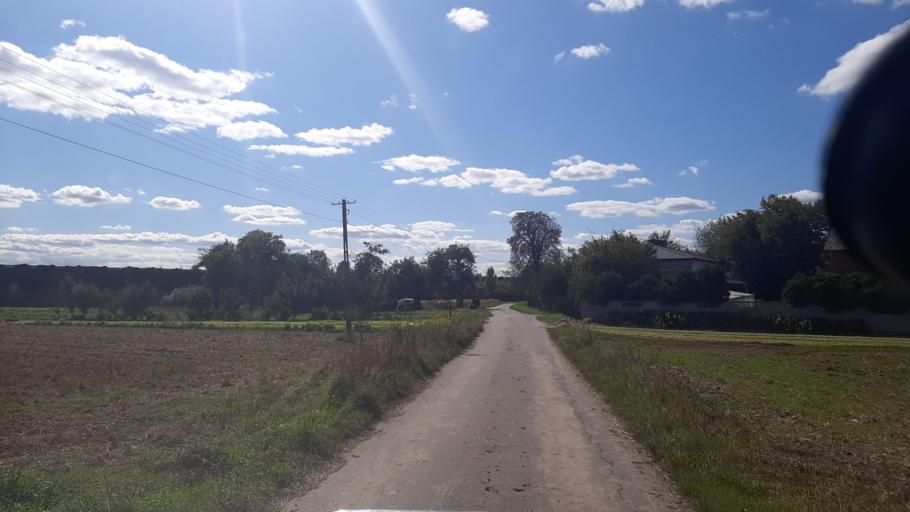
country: PL
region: Lublin Voivodeship
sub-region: Powiat pulawski
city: Markuszow
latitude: 51.3959
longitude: 22.2278
